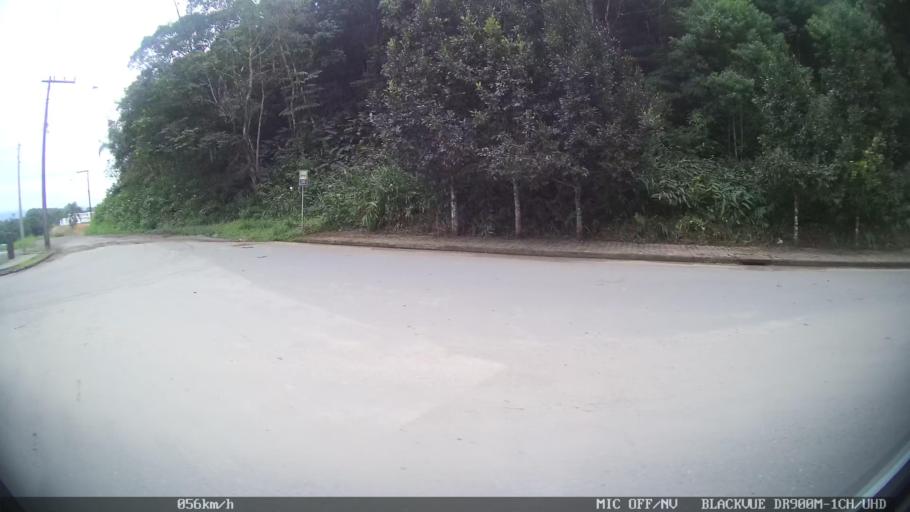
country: BR
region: Santa Catarina
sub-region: Joinville
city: Joinville
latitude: -26.3574
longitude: -48.7990
